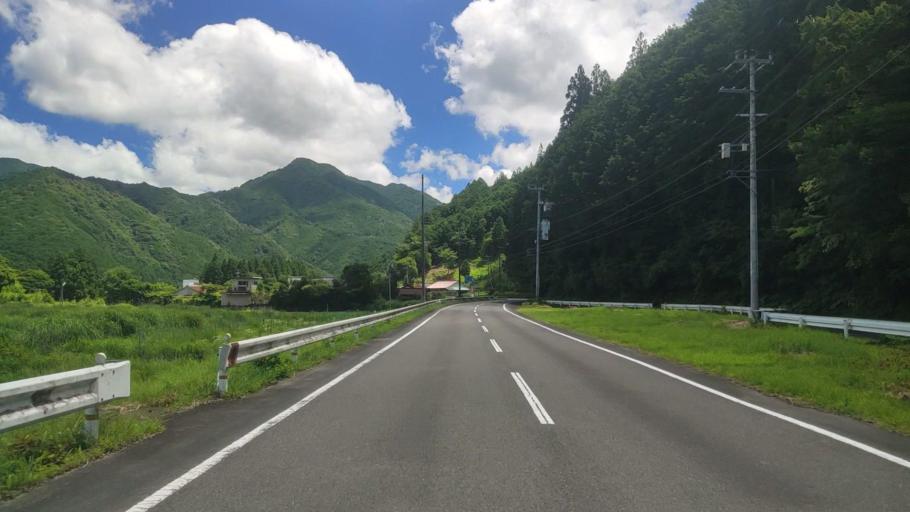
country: JP
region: Mie
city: Owase
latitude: 33.9821
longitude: 136.0367
